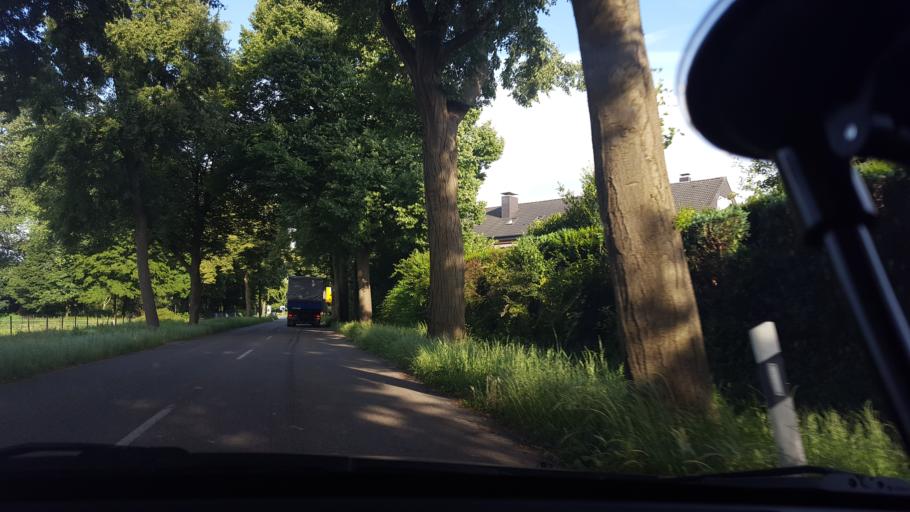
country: DE
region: North Rhine-Westphalia
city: Marl
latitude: 51.6573
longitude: 7.0645
